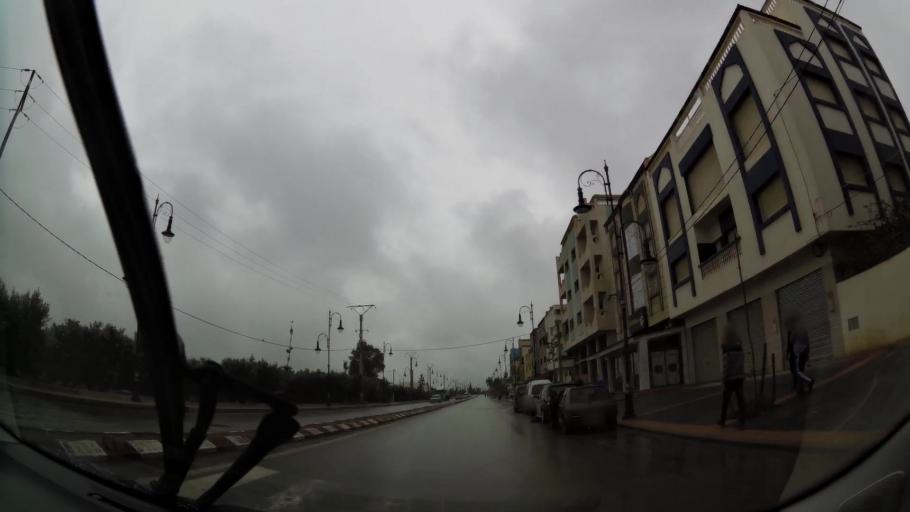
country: MA
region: Taza-Al Hoceima-Taounate
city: Imzourene
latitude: 35.1713
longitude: -3.8622
